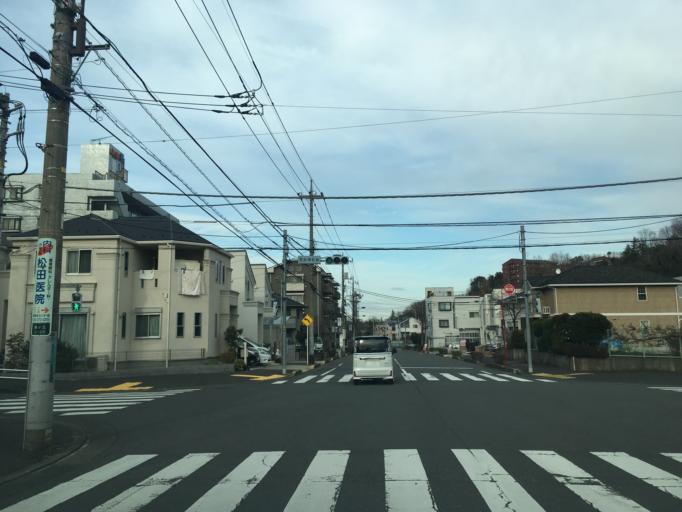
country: JP
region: Tokyo
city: Hino
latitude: 35.6270
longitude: 139.4382
